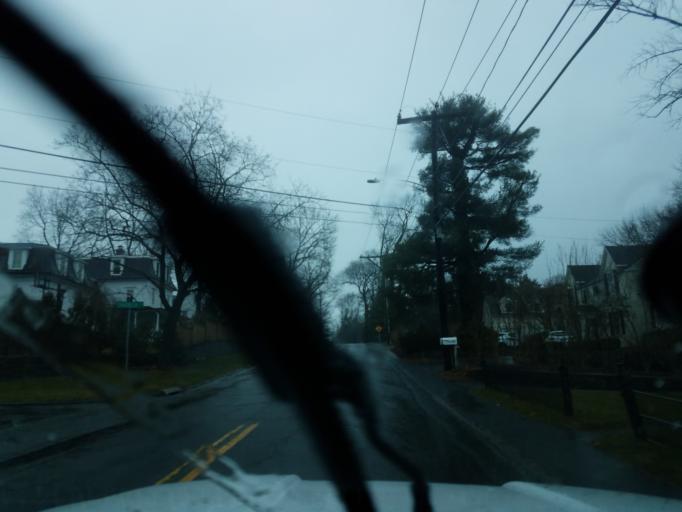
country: US
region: Connecticut
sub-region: Fairfield County
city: Darien
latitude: 41.0784
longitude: -73.4743
